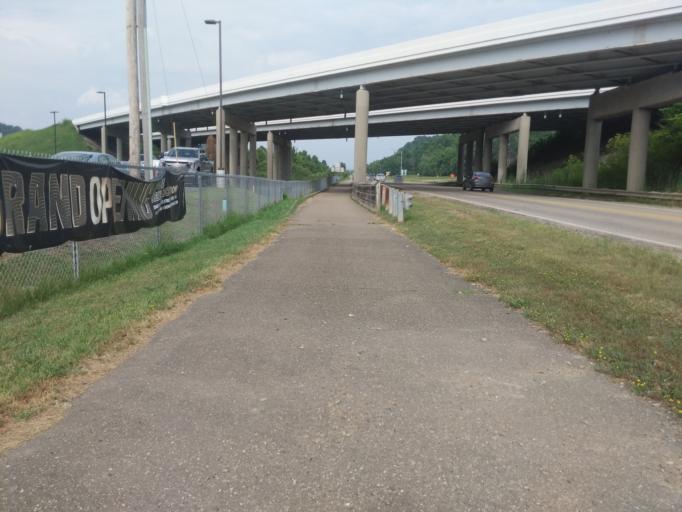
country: US
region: Ohio
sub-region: Athens County
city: Athens
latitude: 39.3343
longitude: -82.0338
